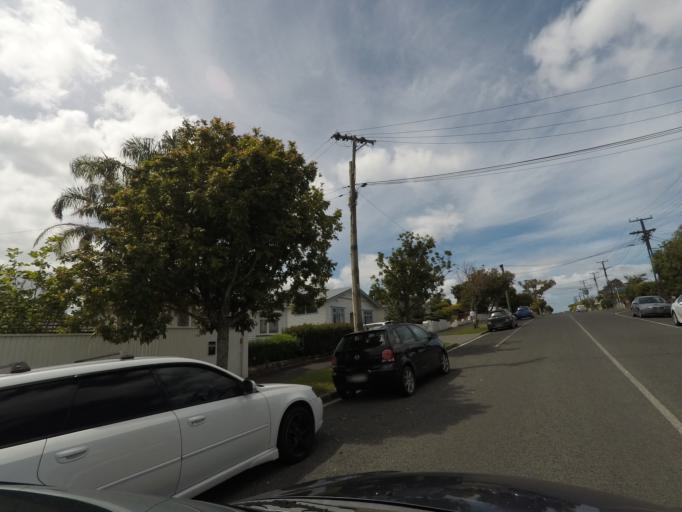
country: NZ
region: Auckland
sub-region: Auckland
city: Rosebank
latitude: -36.8555
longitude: 174.7154
